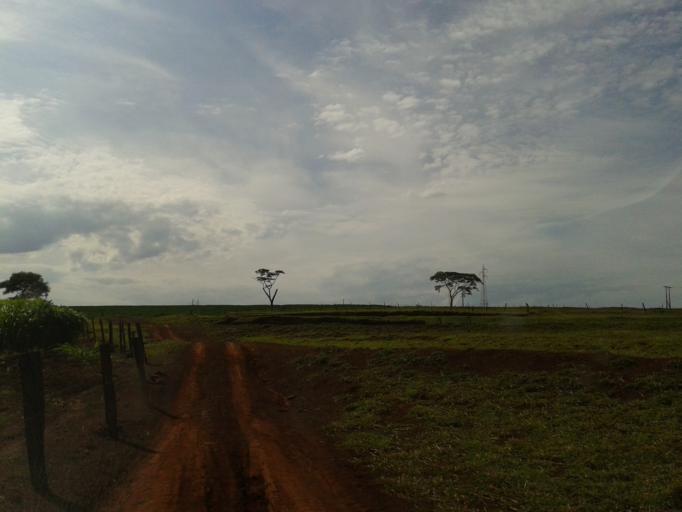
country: BR
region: Minas Gerais
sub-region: Centralina
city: Centralina
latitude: -18.7080
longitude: -49.2088
